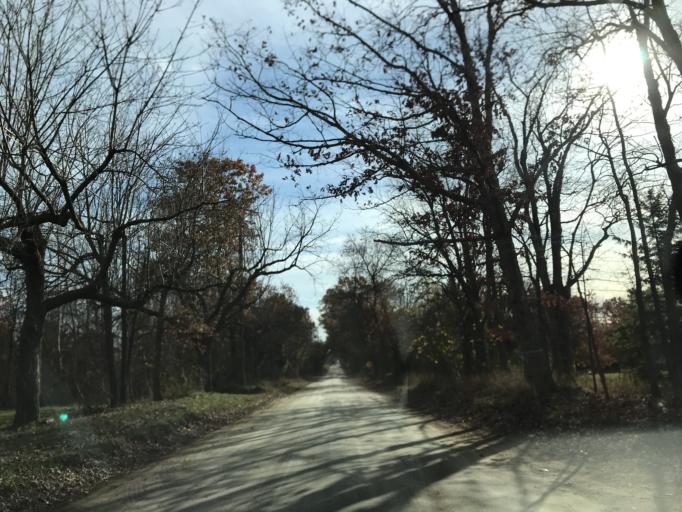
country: US
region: Michigan
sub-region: Oakland County
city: South Lyon
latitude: 42.4847
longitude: -83.6381
